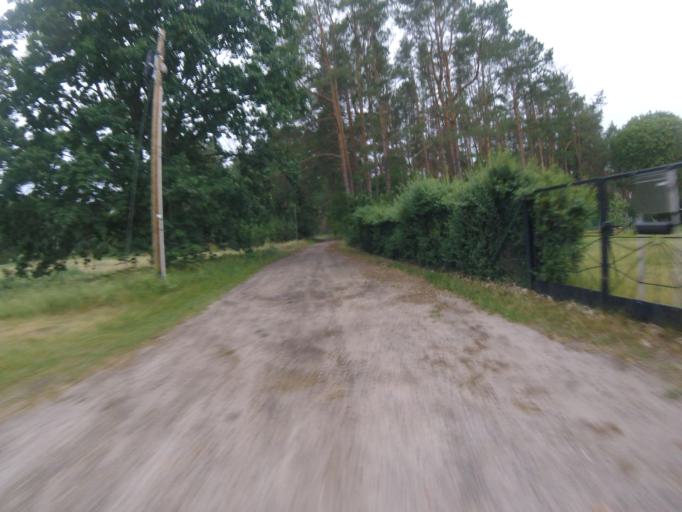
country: DE
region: Brandenburg
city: Bestensee
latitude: 52.2309
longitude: 13.7196
